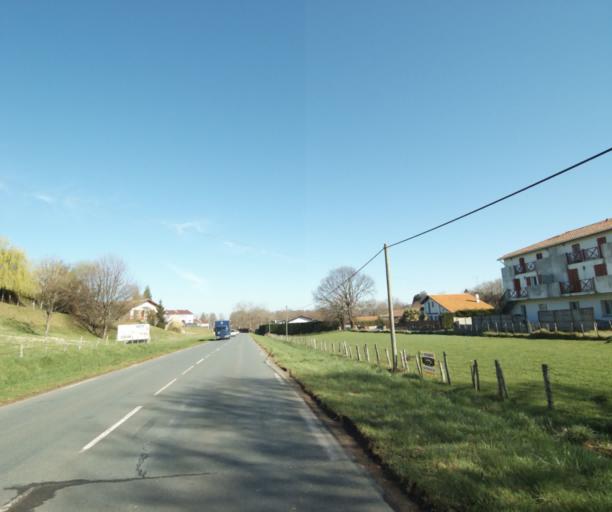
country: FR
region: Aquitaine
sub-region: Departement des Pyrenees-Atlantiques
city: Urrugne
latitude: 43.3433
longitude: -1.6902
